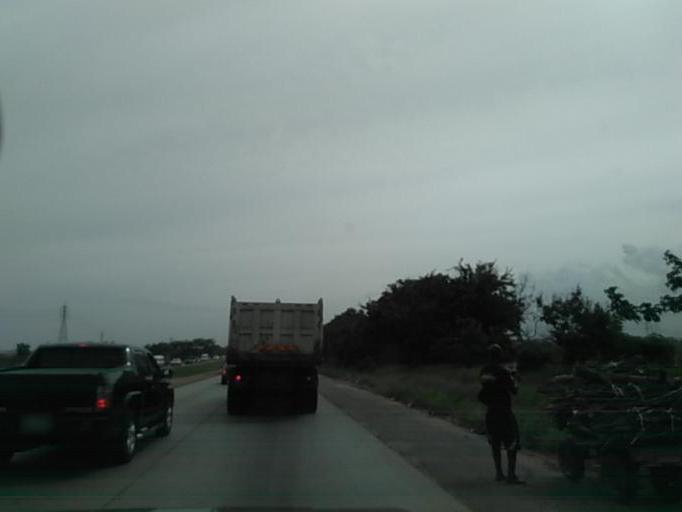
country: GH
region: Greater Accra
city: Tema
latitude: 5.6773
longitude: -0.0386
